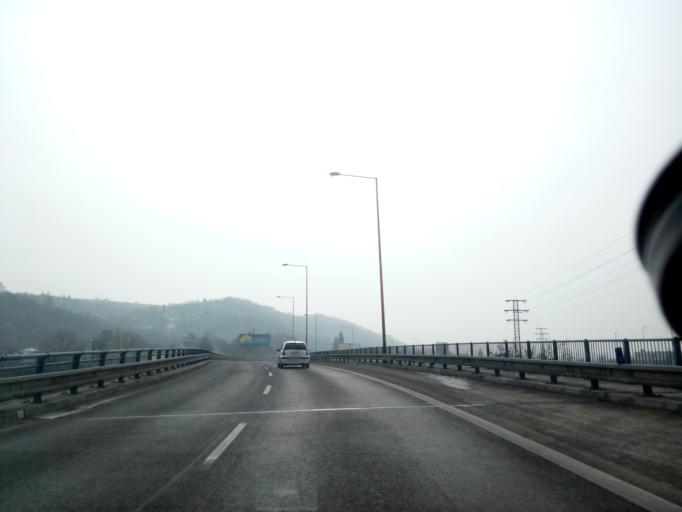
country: SK
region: Kosicky
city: Kosice
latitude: 48.7190
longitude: 21.2764
